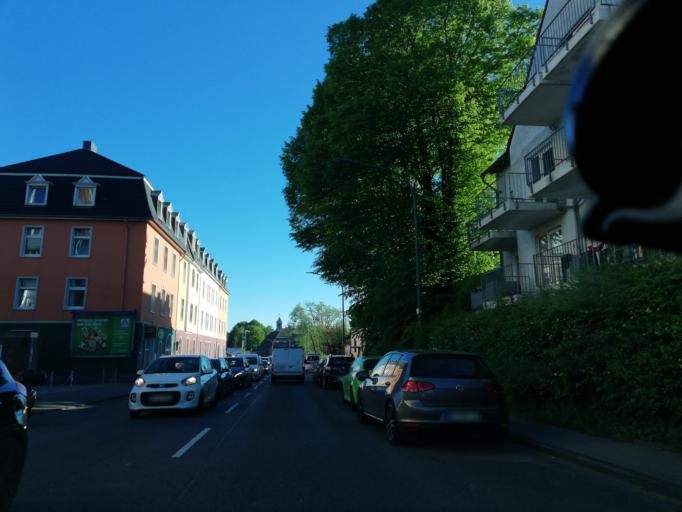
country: DE
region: North Rhine-Westphalia
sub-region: Regierungsbezirk Dusseldorf
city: Wuppertal
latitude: 51.2465
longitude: 7.1921
